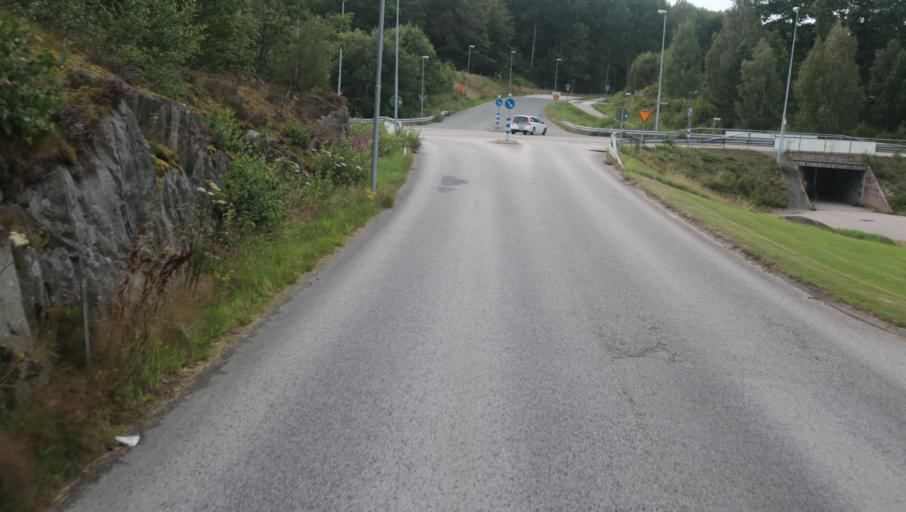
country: SE
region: Blekinge
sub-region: Karlshamns Kommun
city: Karlshamn
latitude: 56.2018
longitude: 14.8517
